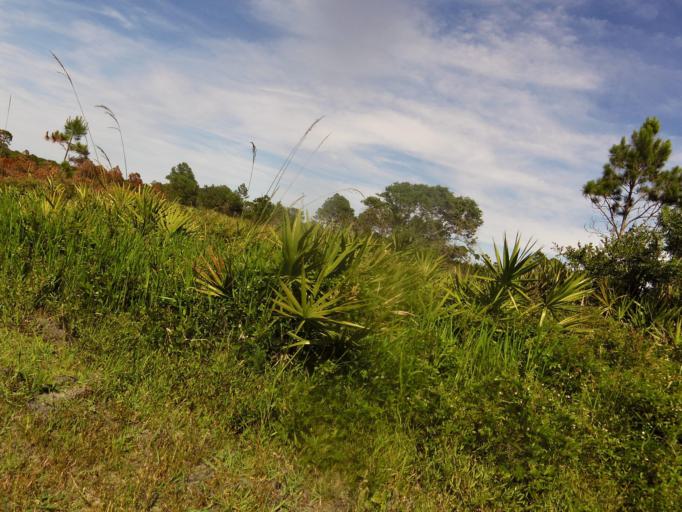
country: US
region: Florida
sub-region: Saint Johns County
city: Villano Beach
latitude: 30.0302
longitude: -81.3439
